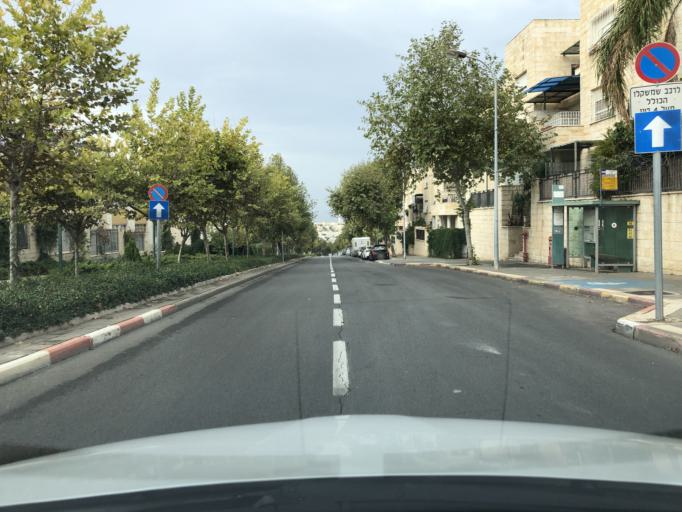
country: IL
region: Central District
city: Modiin
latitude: 31.9131
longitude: 35.0101
